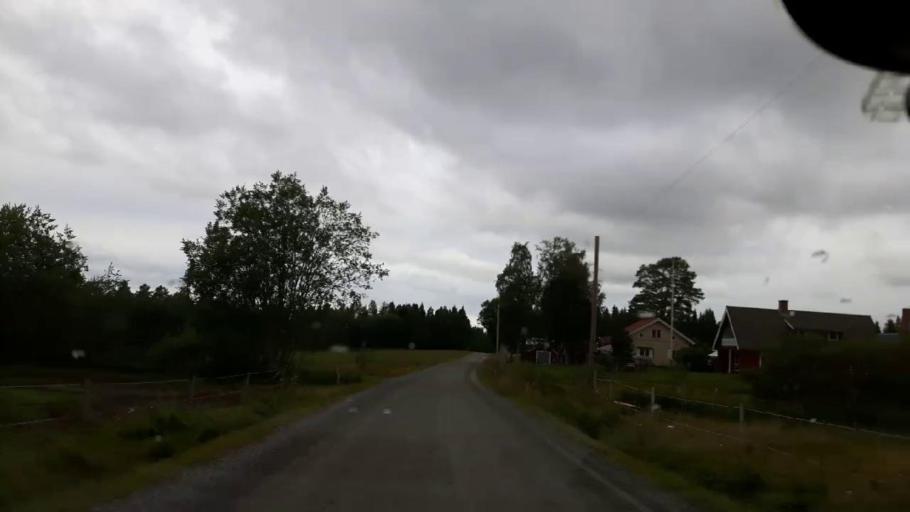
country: SE
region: Jaemtland
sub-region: OEstersunds Kommun
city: Ostersund
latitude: 63.0577
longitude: 14.5582
